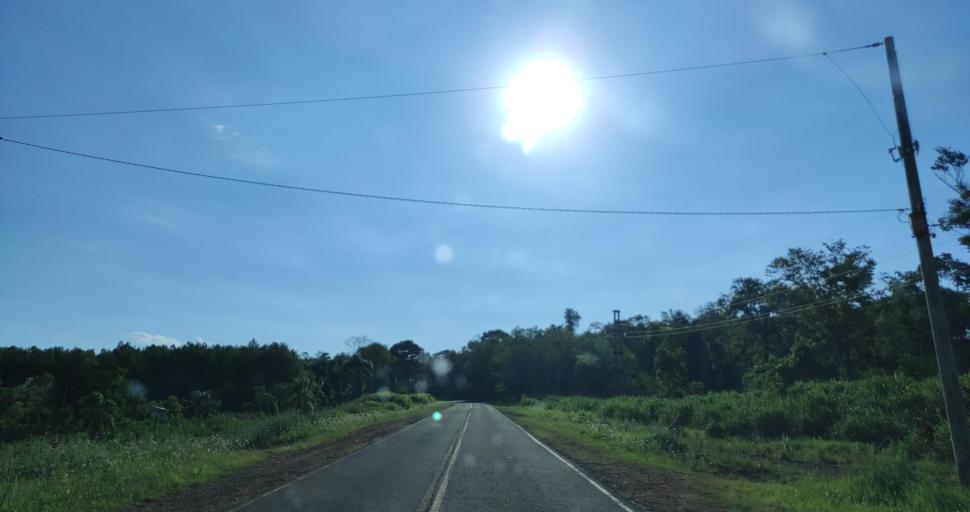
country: AR
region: Misiones
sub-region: Departamento de Eldorado
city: Eldorado
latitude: -26.3729
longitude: -54.3206
